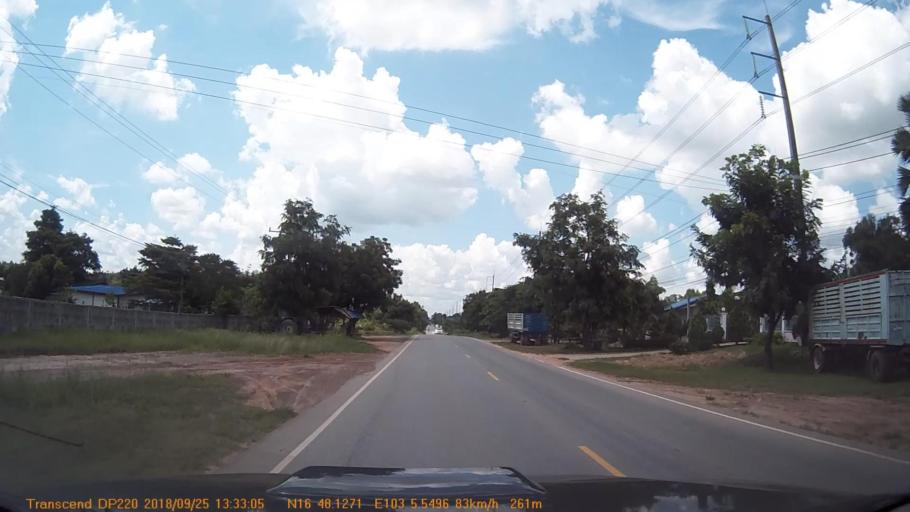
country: TH
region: Khon Kaen
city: Kranuan
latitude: 16.8022
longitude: 103.0924
